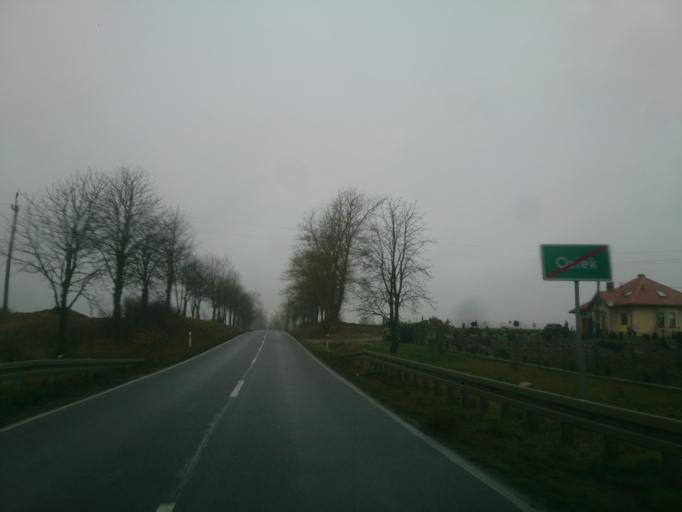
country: PL
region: Kujawsko-Pomorskie
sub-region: Powiat brodnicki
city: Brodnica
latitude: 53.1773
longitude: 19.3884
